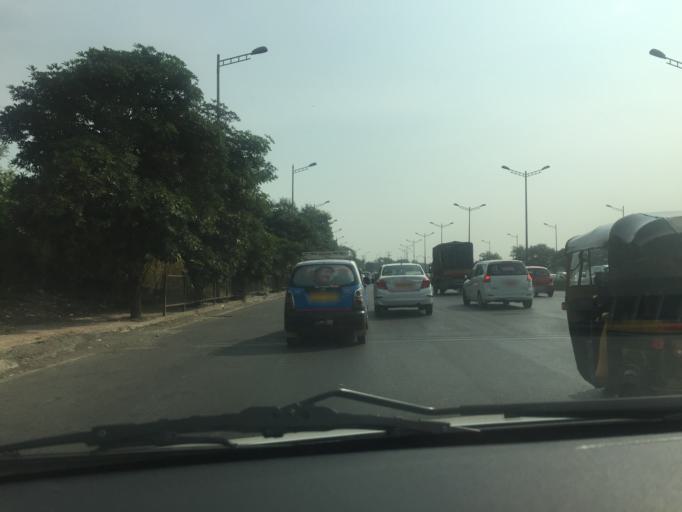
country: IN
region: Maharashtra
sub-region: Mumbai Suburban
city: Powai
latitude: 19.1251
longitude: 72.9343
